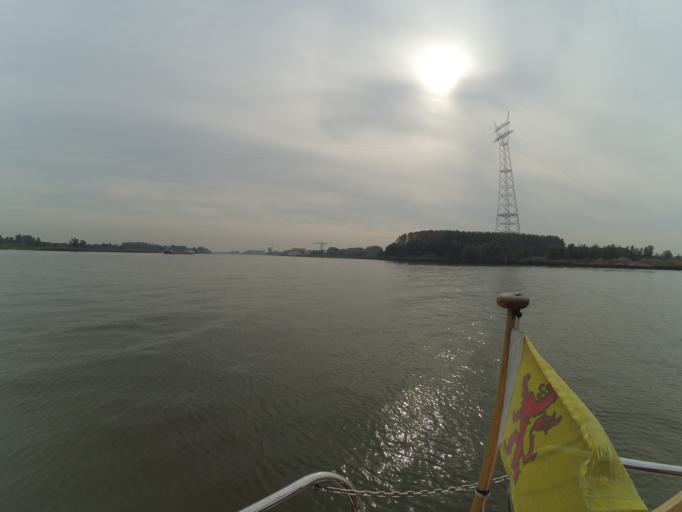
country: NL
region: South Holland
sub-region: Gemeente Krimpen aan den IJssel
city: Krimpen aan den IJssel
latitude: 51.8947
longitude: 4.5919
